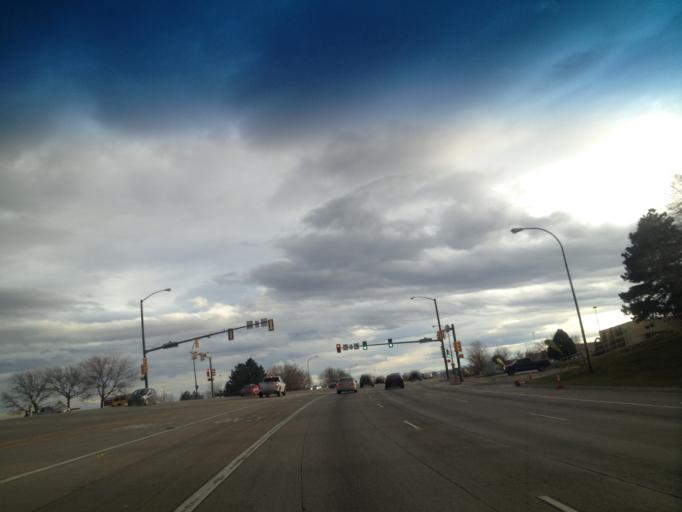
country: US
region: Colorado
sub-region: Adams County
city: Westminster
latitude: 39.8602
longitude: -105.0819
